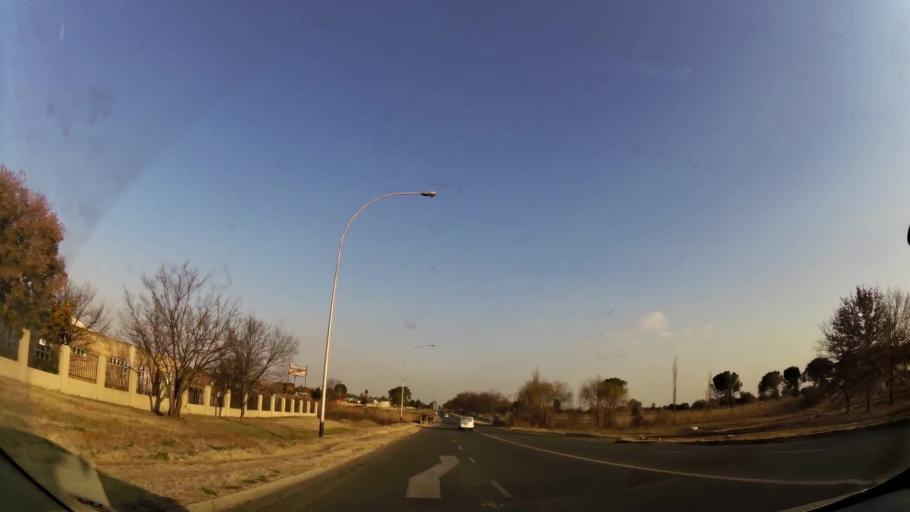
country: ZA
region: Gauteng
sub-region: Ekurhuleni Metropolitan Municipality
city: Germiston
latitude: -26.2738
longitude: 28.2256
